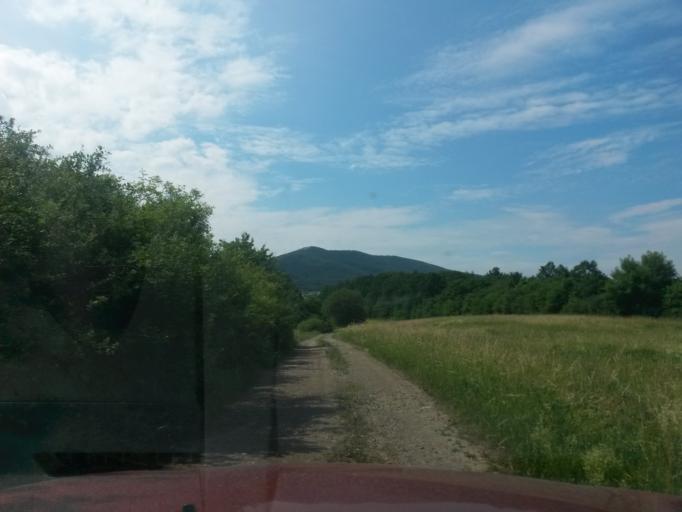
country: SK
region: Kosicky
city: Secovce
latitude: 48.6269
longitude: 21.4996
